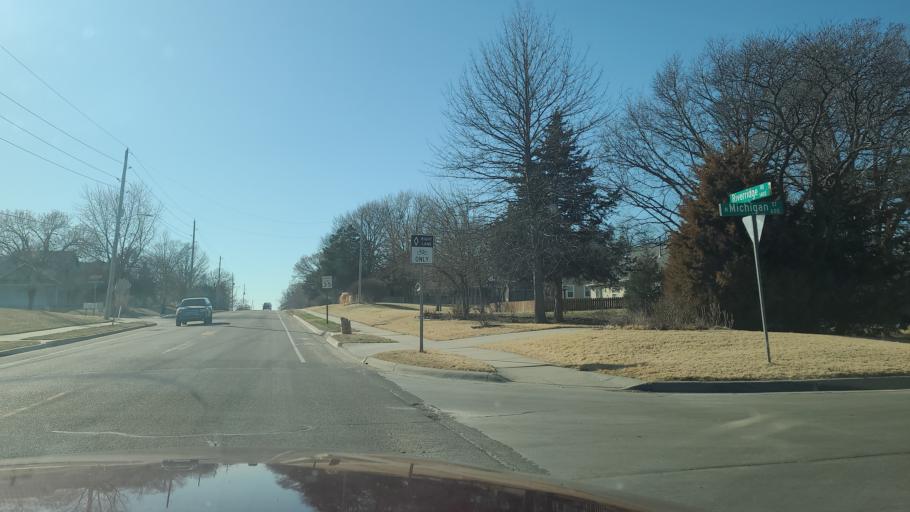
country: US
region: Kansas
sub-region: Douglas County
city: Lawrence
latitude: 38.9934
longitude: -95.2518
